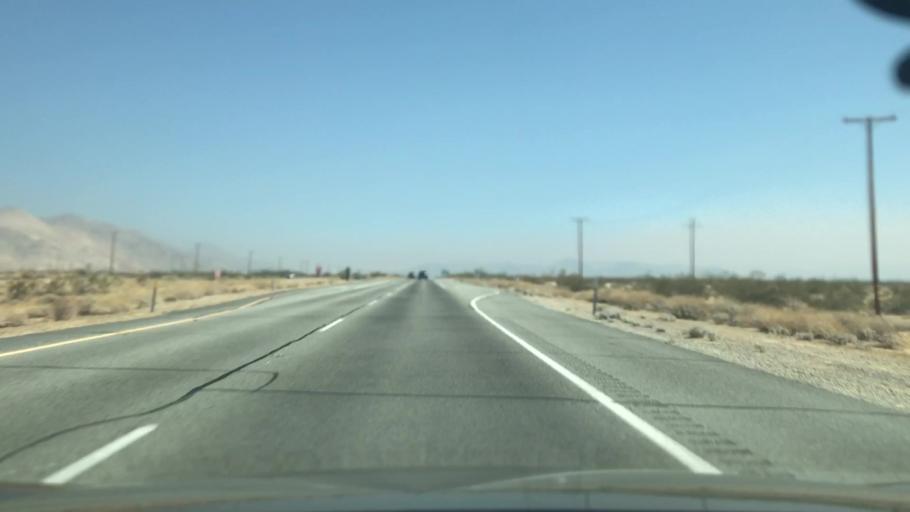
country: US
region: California
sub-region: Kern County
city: Inyokern
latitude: 35.7238
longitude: -117.8687
